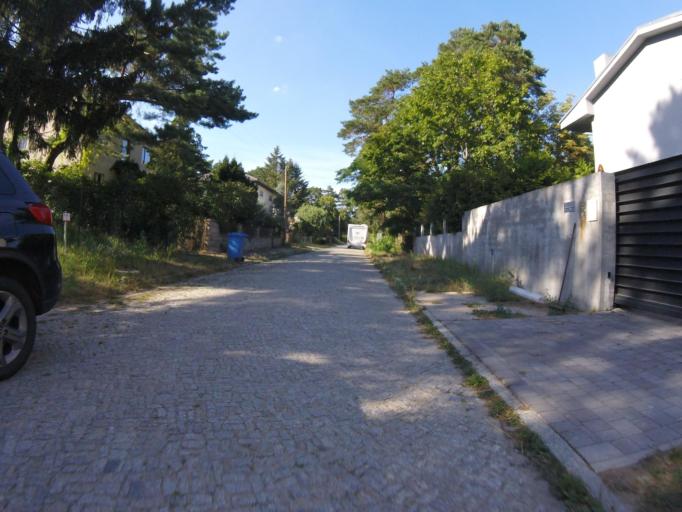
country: DE
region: Brandenburg
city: Wildau
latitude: 52.3112
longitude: 13.6972
